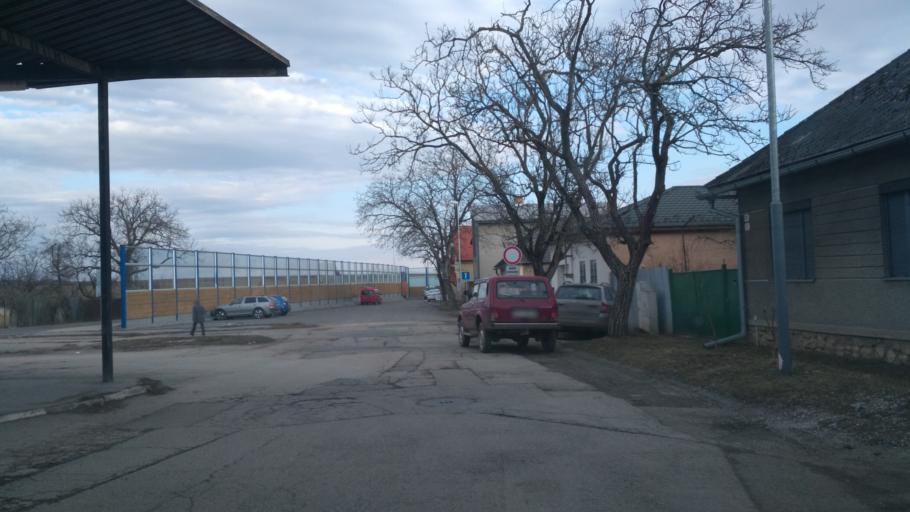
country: SK
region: Kosicky
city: Moldava nad Bodvou
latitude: 48.6093
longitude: 21.0022
